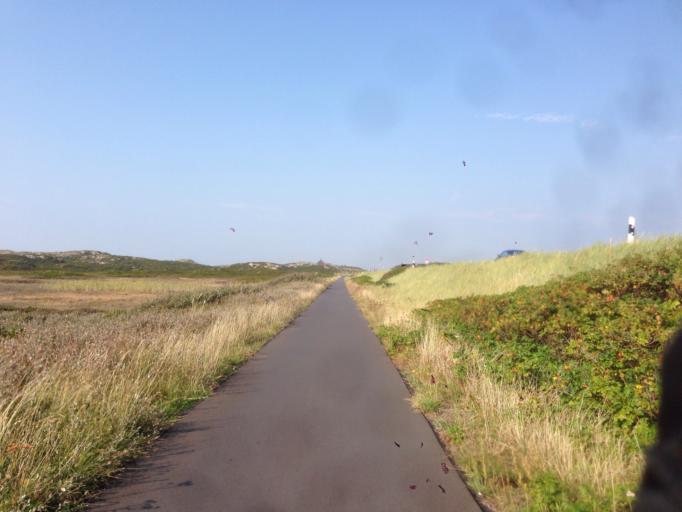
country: DE
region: Schleswig-Holstein
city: Westerland
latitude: 54.8331
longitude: 8.2914
